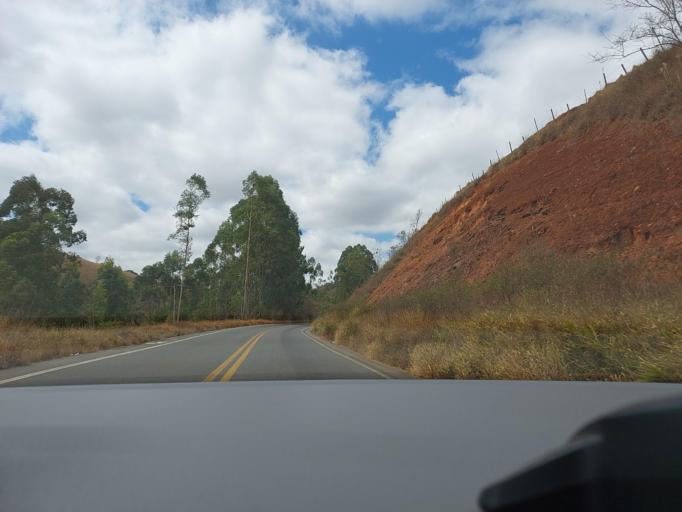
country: BR
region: Minas Gerais
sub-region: Vicosa
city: Vicosa
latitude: -20.8364
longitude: -42.7217
